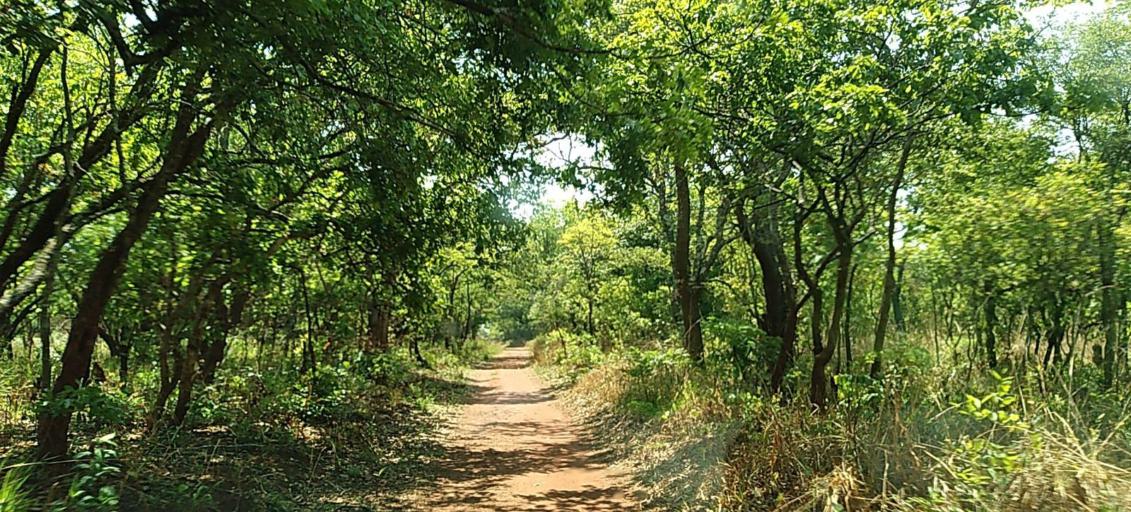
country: CD
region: Katanga
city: Kolwezi
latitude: -11.2818
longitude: 25.1397
